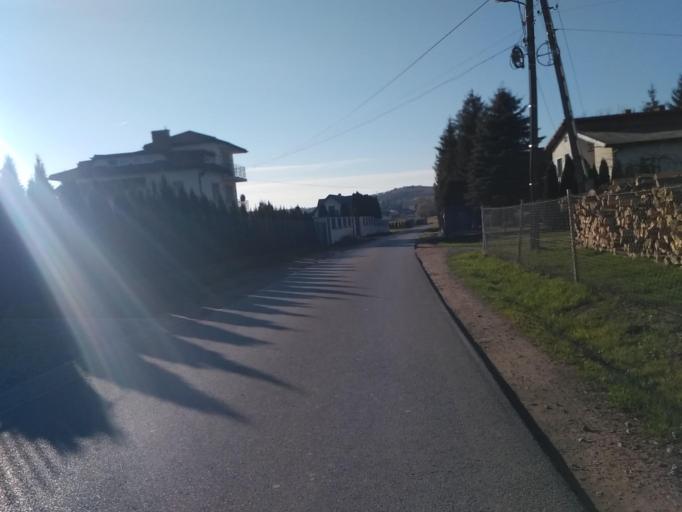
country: PL
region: Subcarpathian Voivodeship
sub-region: Powiat brzozowski
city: Humniska
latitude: 49.6776
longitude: 22.0427
